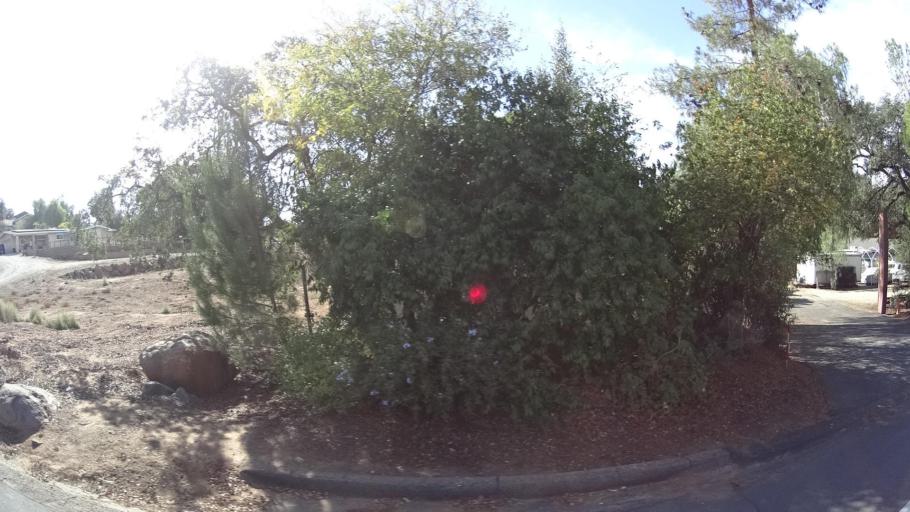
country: US
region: California
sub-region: San Diego County
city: Alpine
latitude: 32.8190
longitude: -116.7930
